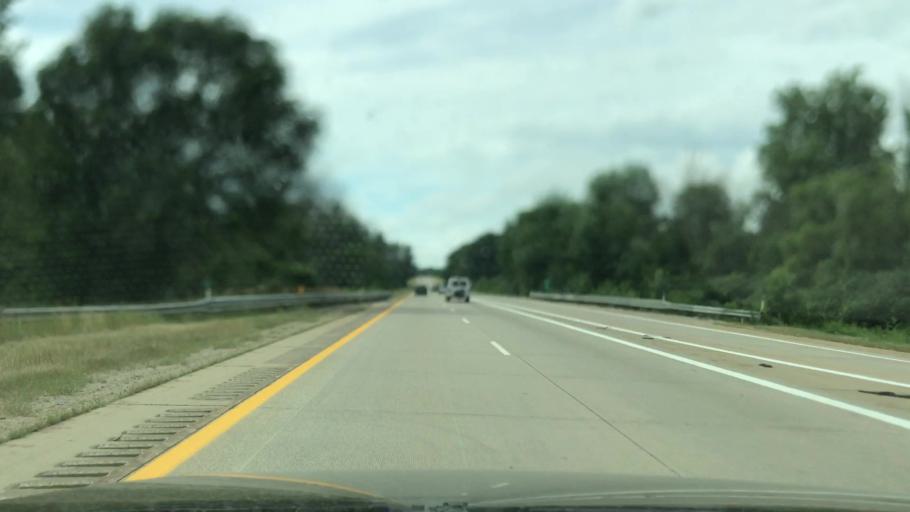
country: US
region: Michigan
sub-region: Kent County
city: Walker
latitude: 43.0199
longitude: -85.7687
